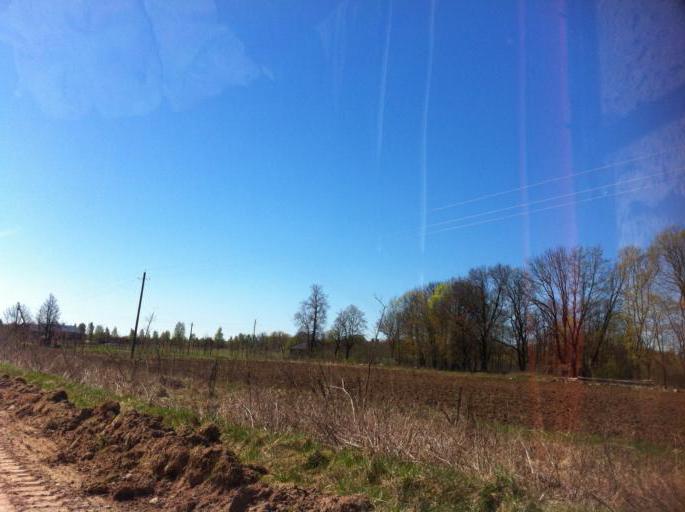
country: RU
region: Pskov
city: Izborsk
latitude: 57.8111
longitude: 27.9795
